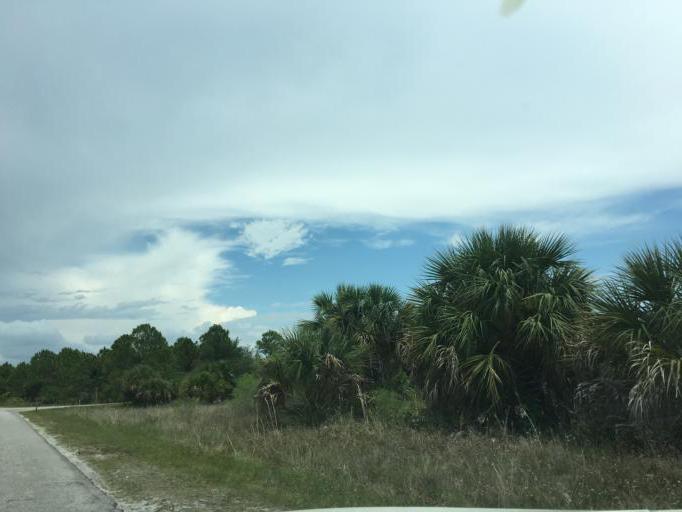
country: US
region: Florida
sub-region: Pinellas County
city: Palm Harbor
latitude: 28.0596
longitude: -82.8223
